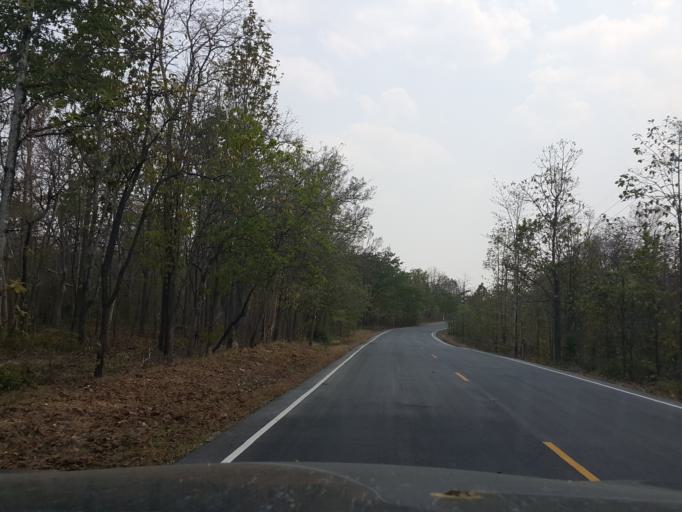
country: TH
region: Lampang
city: Mae Phrik
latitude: 17.4829
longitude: 99.1183
